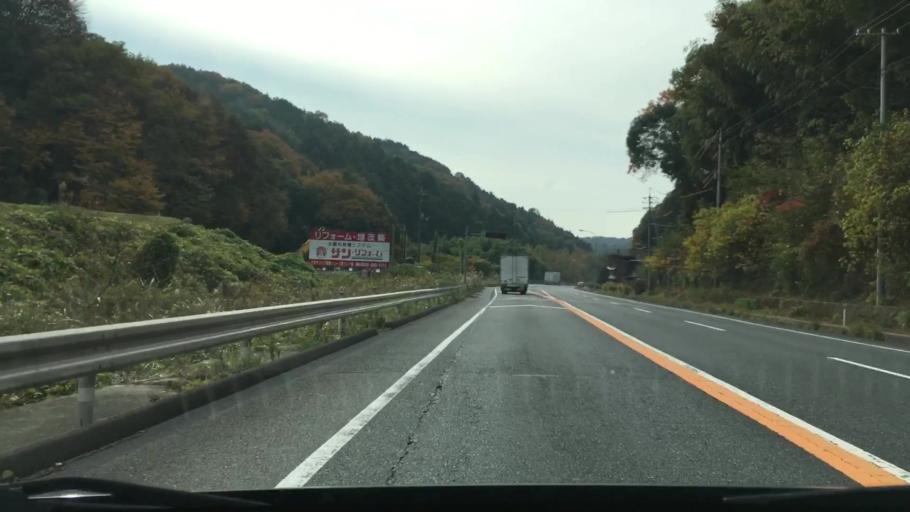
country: JP
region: Yamaguchi
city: Hikari
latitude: 34.0701
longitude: 131.9840
